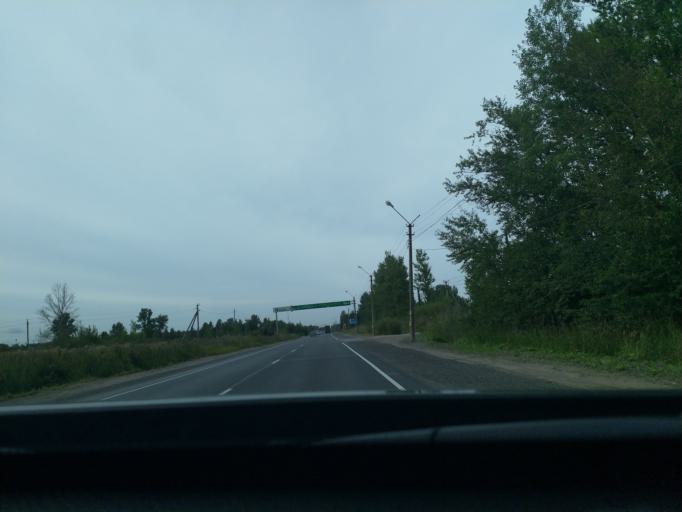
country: RU
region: Leningrad
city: Nikol'skoye
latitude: 59.7202
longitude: 30.7787
